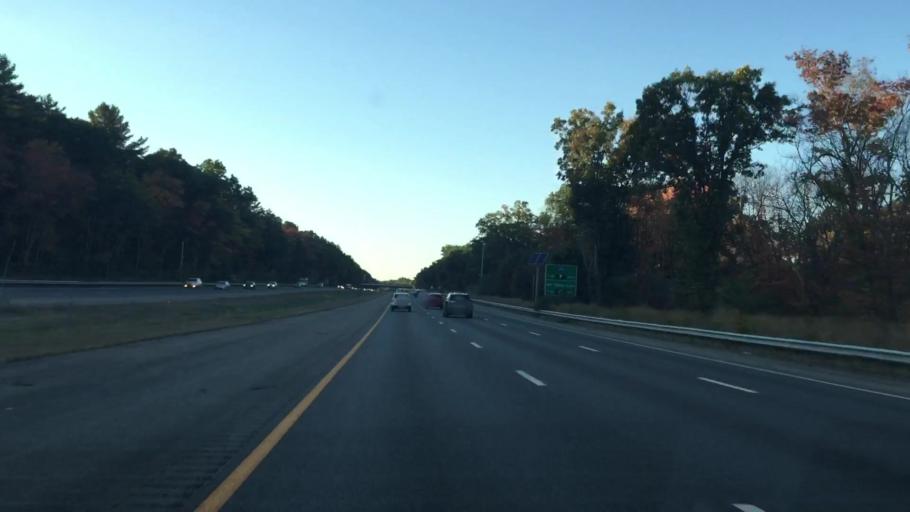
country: US
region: Massachusetts
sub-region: Middlesex County
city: Pinehurst
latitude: 42.5089
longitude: -71.2499
